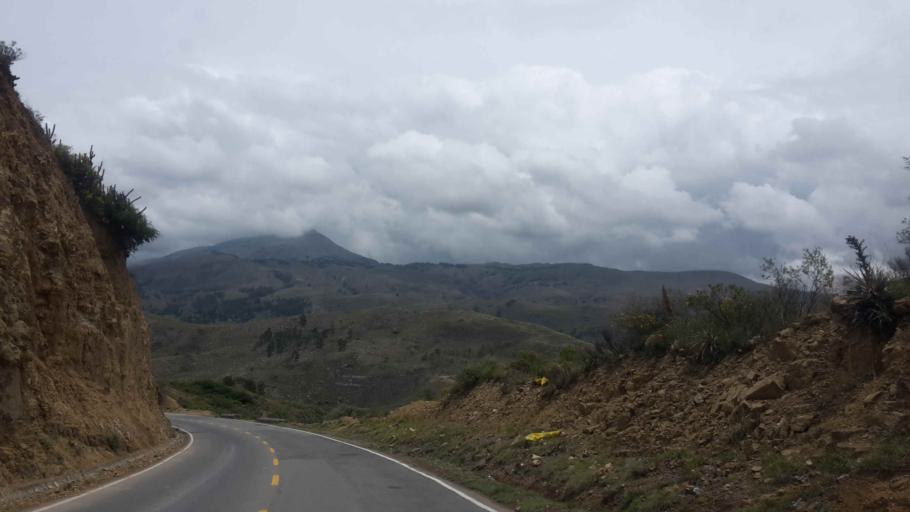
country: BO
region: Cochabamba
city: Punata
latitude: -17.4910
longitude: -65.7854
